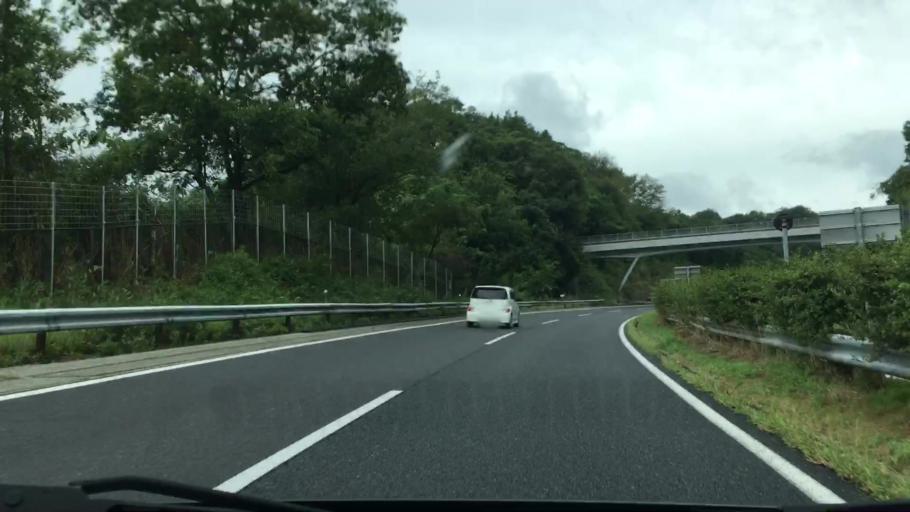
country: JP
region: Okayama
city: Tsuyama
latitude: 35.0171
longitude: 134.2153
